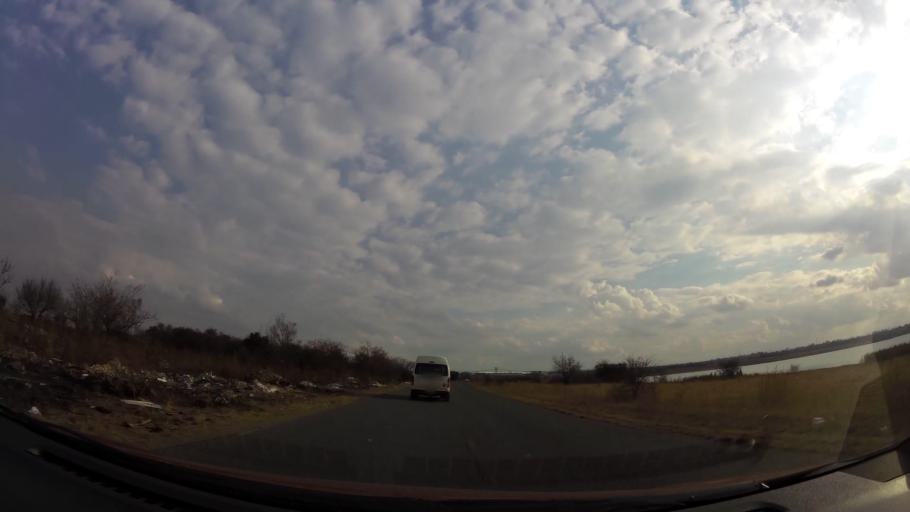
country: ZA
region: Gauteng
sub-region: Sedibeng District Municipality
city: Vereeniging
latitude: -26.6914
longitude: 27.8979
